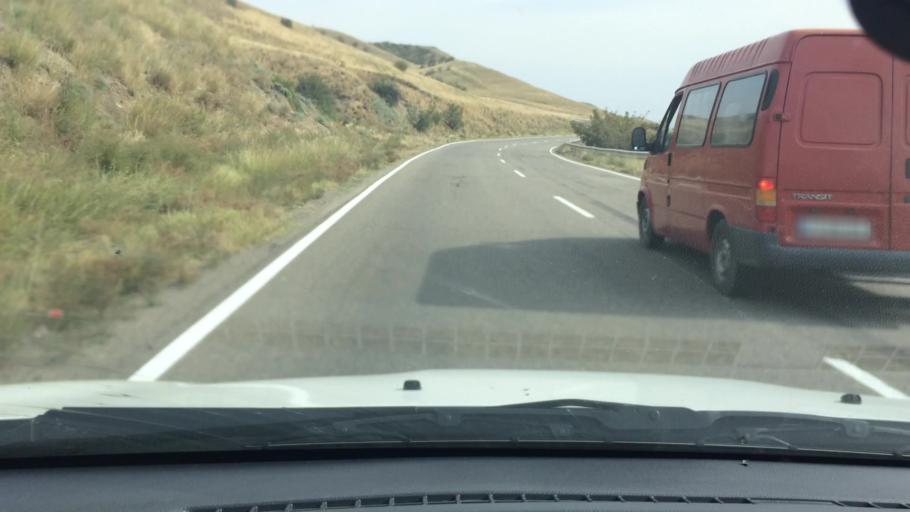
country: GE
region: Kvemo Kartli
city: Rust'avi
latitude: 41.4984
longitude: 44.9596
